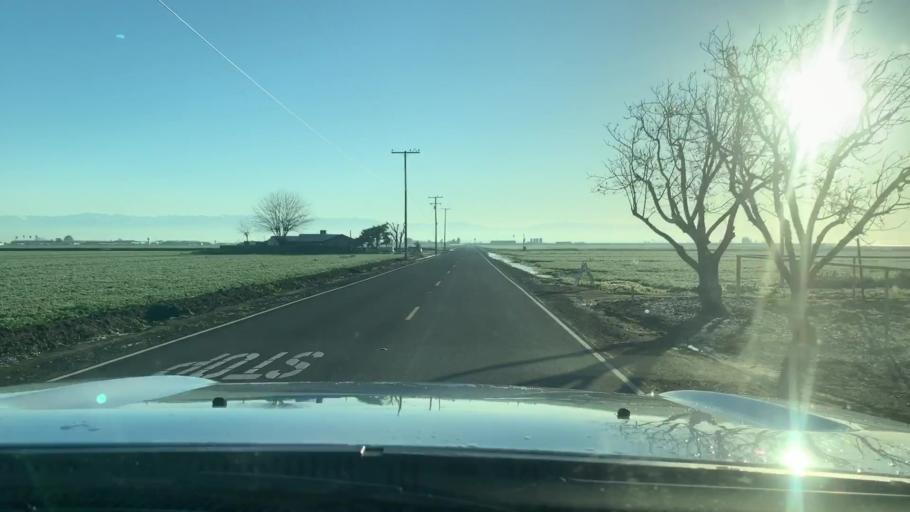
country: US
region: California
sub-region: Kings County
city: Corcoran
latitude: 36.2033
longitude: -119.4910
